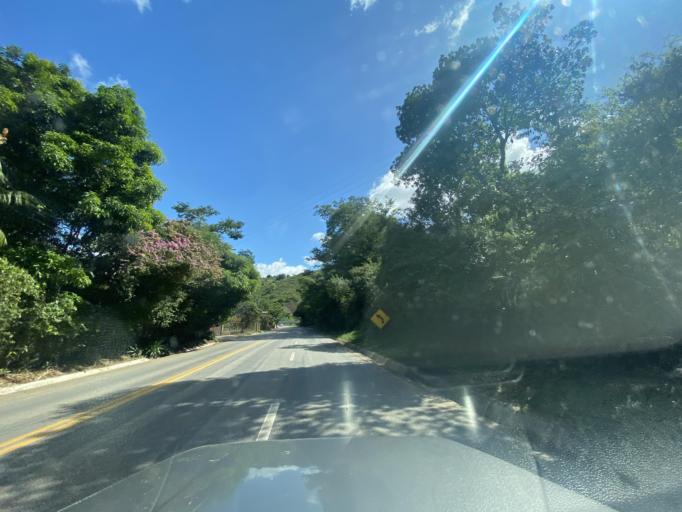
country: BR
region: Espirito Santo
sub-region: Alegre
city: Alegre
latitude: -20.7613
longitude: -41.5148
